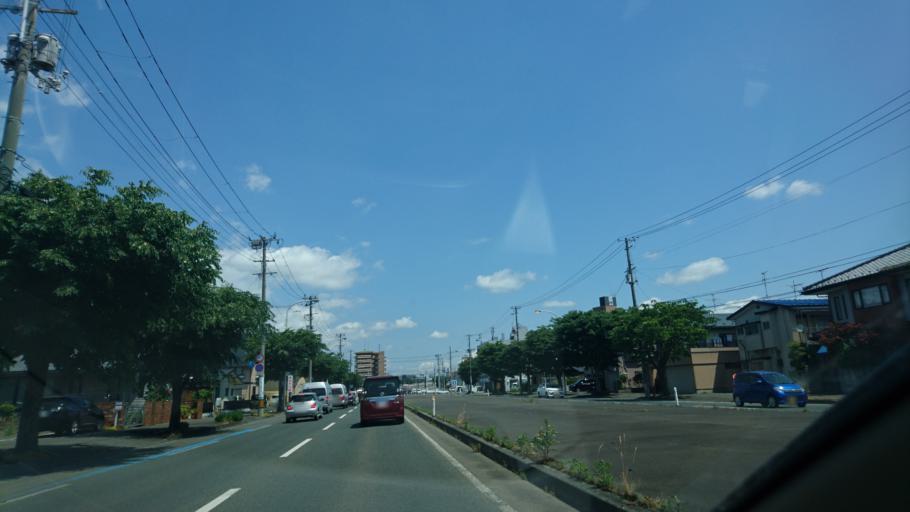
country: JP
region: Iwate
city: Morioka-shi
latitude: 39.6870
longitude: 141.1356
